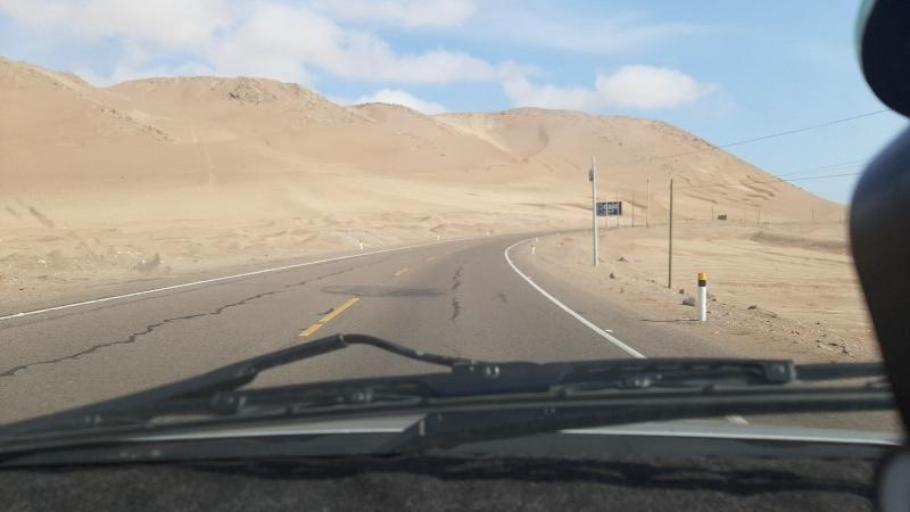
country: PE
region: Moquegua
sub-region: Provincia de Ilo
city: El Algarrobal
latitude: -17.6636
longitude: -71.2946
